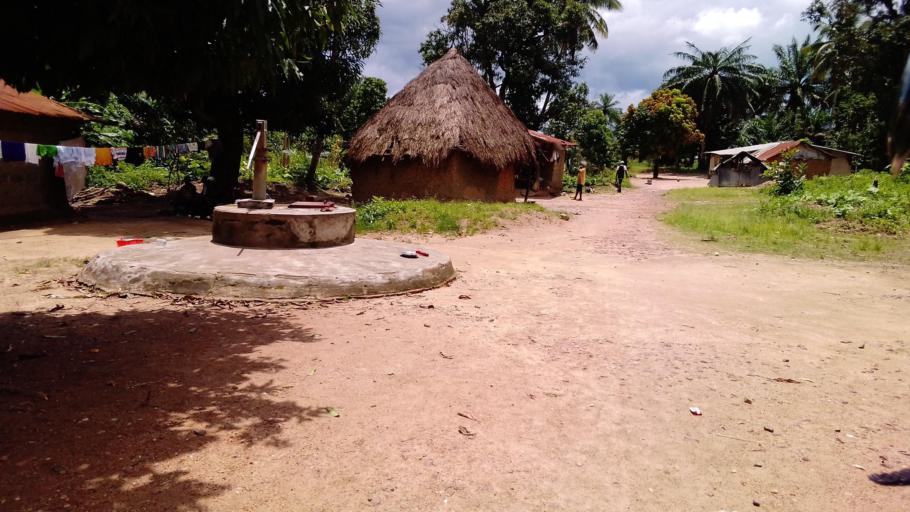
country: SL
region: Eastern Province
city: Koidu
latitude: 8.6688
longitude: -10.9540
